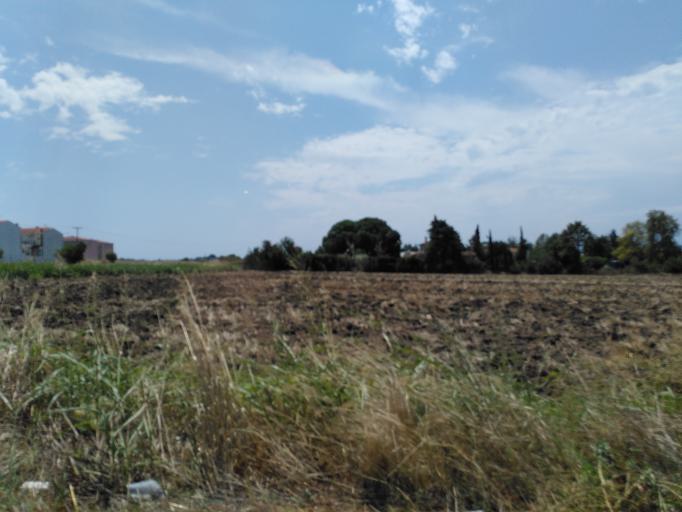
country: GR
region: Central Macedonia
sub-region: Nomos Thessalonikis
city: Epanomi
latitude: 40.4314
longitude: 22.9181
